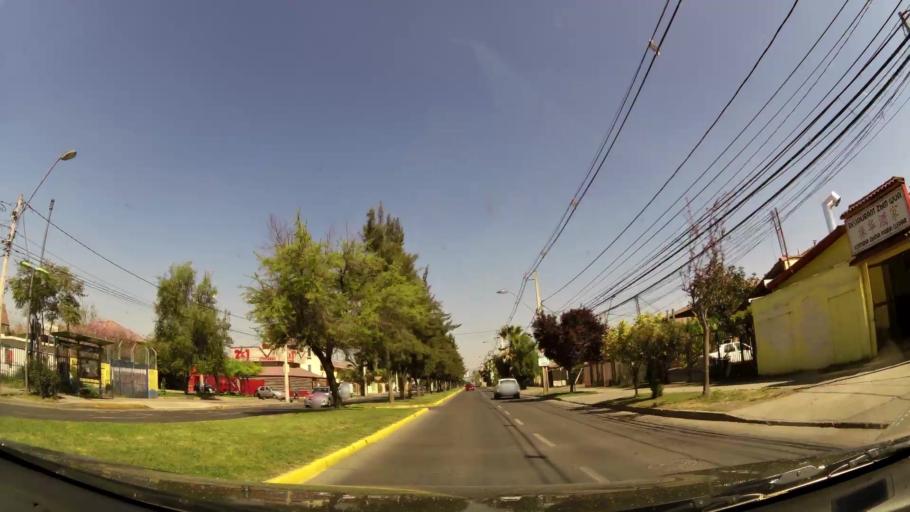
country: CL
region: Santiago Metropolitan
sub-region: Provincia de Santiago
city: Lo Prado
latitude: -33.3507
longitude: -70.7290
